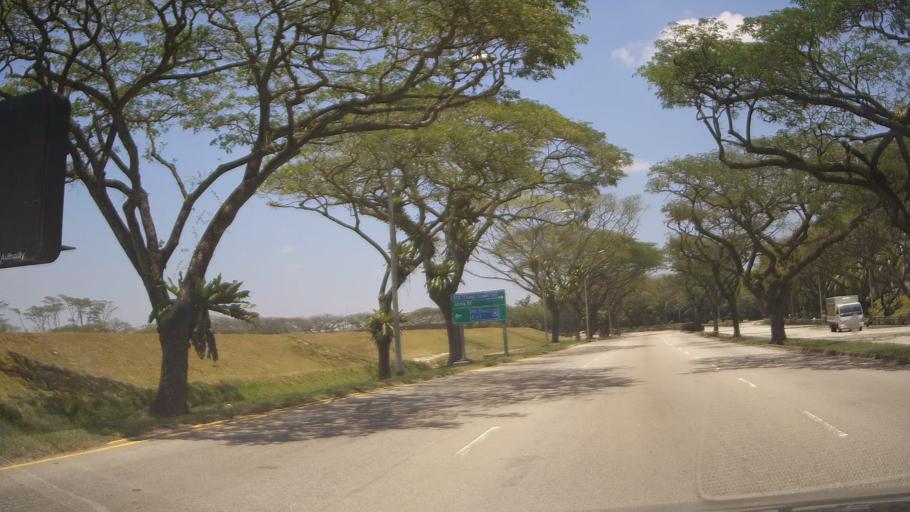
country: MY
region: Johor
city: Johor Bahru
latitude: 1.3537
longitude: 103.7150
